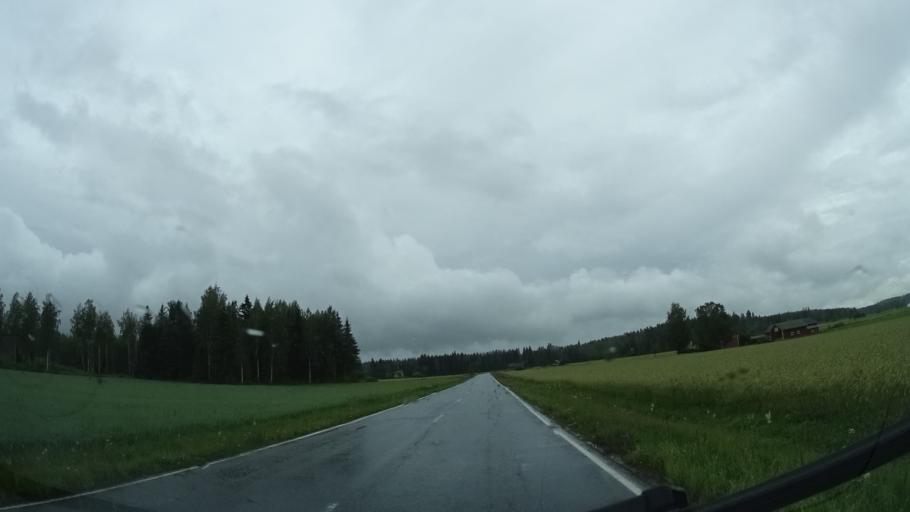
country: FI
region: Haeme
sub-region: Forssa
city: Humppila
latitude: 60.9837
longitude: 23.2535
